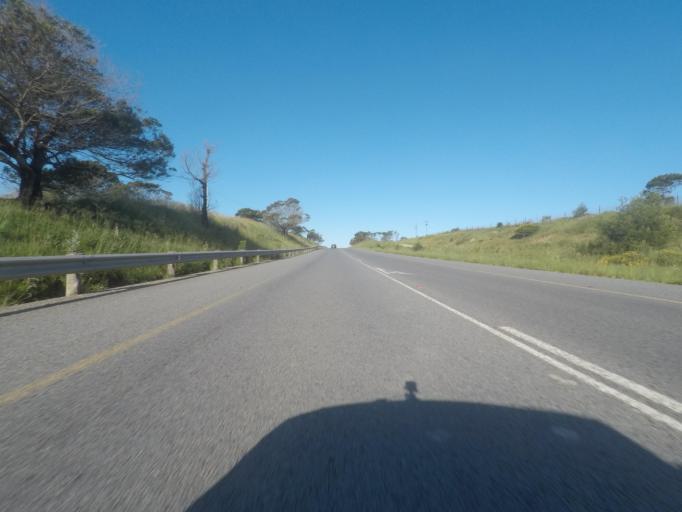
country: ZA
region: Eastern Cape
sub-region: Buffalo City Metropolitan Municipality
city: East London
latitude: -33.0585
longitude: 27.7942
